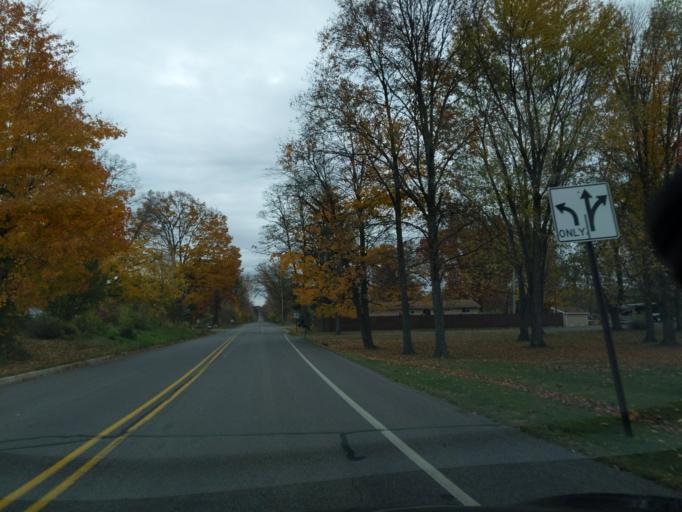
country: US
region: Michigan
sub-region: Jackson County
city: Spring Arbor
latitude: 42.2766
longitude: -84.5389
